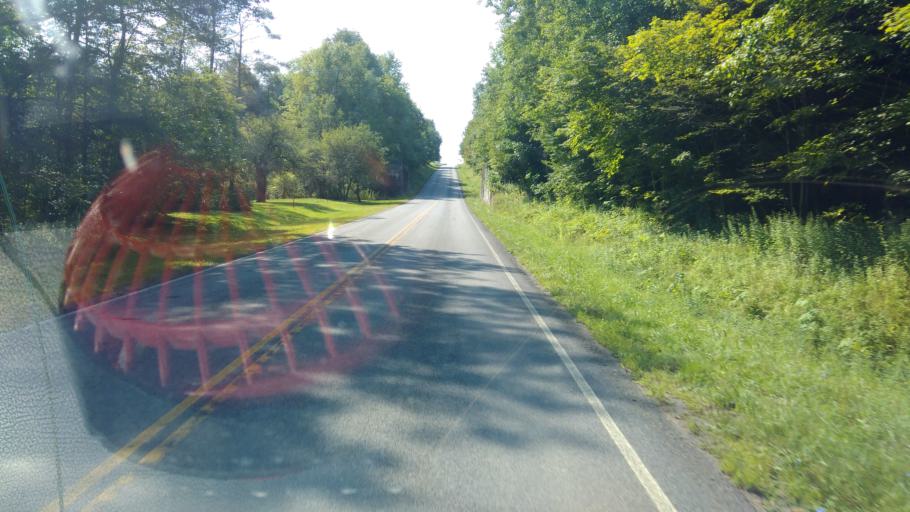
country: US
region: New York
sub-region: Allegany County
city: Friendship
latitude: 42.1649
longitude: -78.1496
